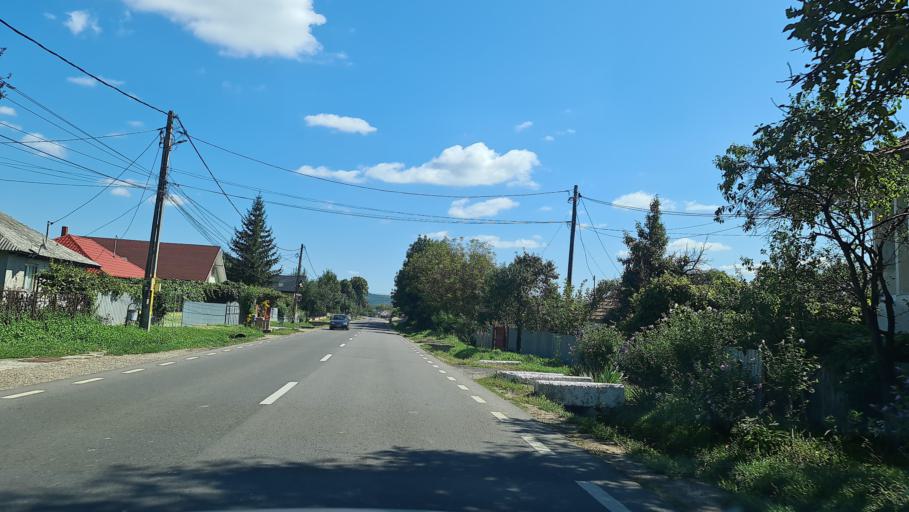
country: RO
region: Bacau
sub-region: Comuna Ardeoani
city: Ardeoani
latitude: 46.5333
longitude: 26.6235
